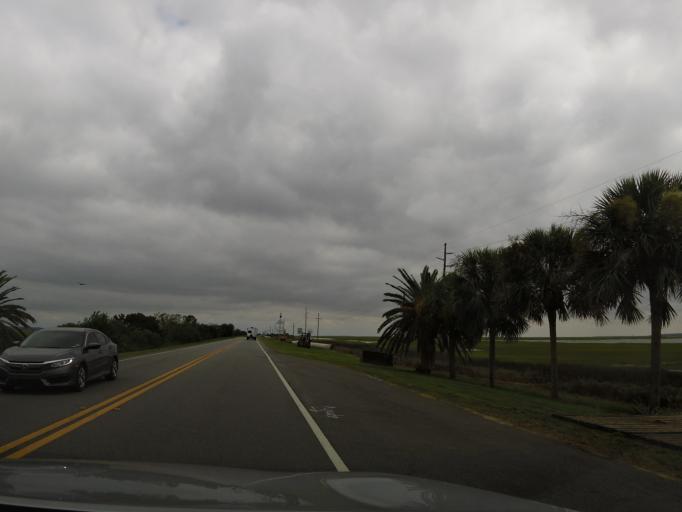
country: US
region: Georgia
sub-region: Glynn County
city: Brunswick
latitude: 31.1023
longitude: -81.4906
